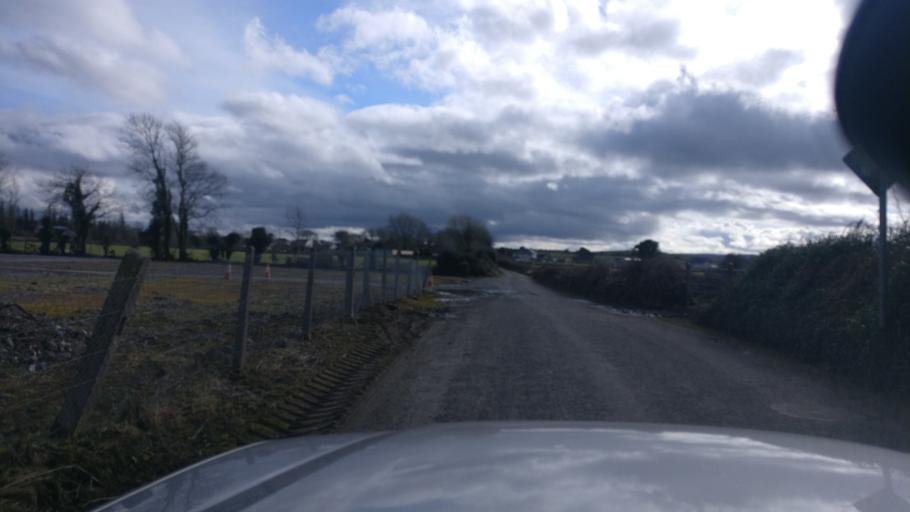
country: IE
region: Connaught
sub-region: County Galway
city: Loughrea
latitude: 53.1961
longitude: -8.5404
